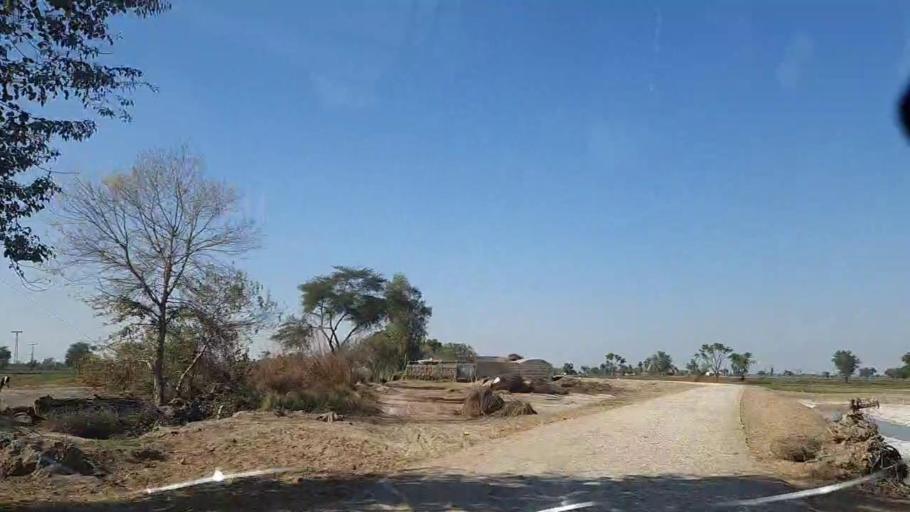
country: PK
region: Sindh
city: Khanpur
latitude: 27.8451
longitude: 69.3971
